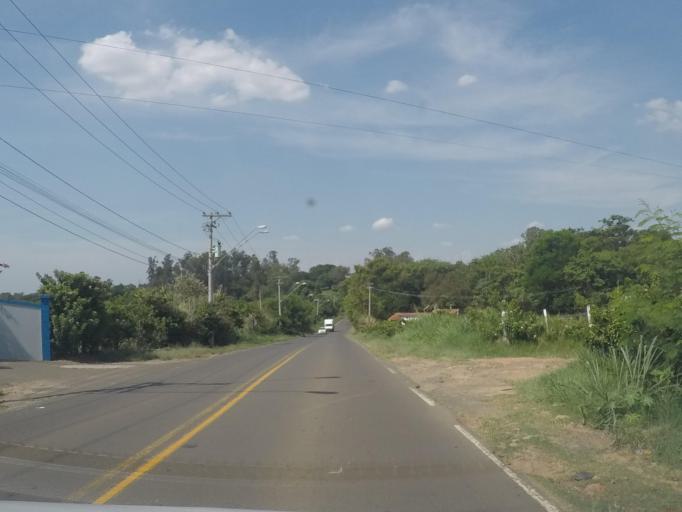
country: BR
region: Sao Paulo
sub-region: Sumare
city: Sumare
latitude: -22.8543
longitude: -47.2877
